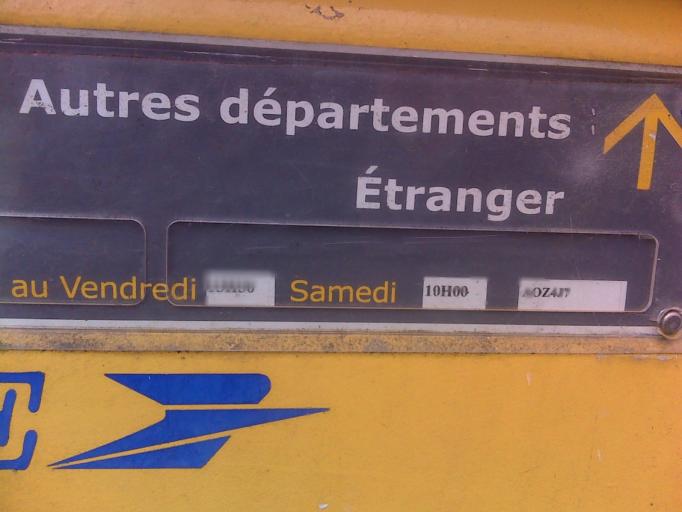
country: FR
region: Lower Normandy
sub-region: Departement de la Manche
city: Avranches
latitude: 48.6866
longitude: -1.3632
